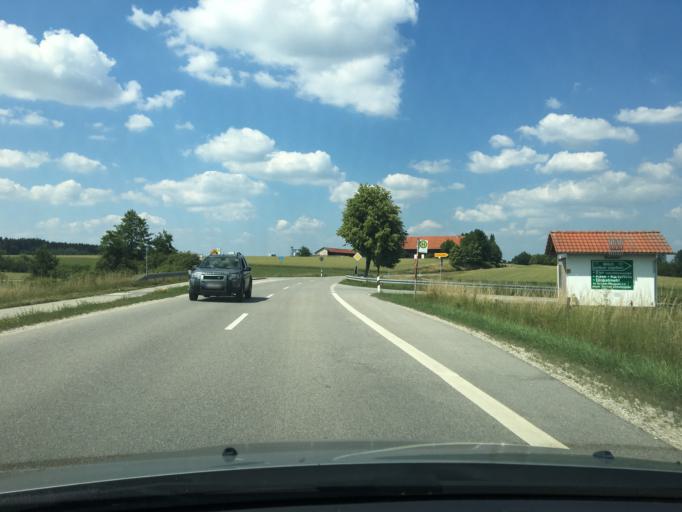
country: DE
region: Bavaria
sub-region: Lower Bavaria
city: Vilsbiburg
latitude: 48.4360
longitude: 12.3438
